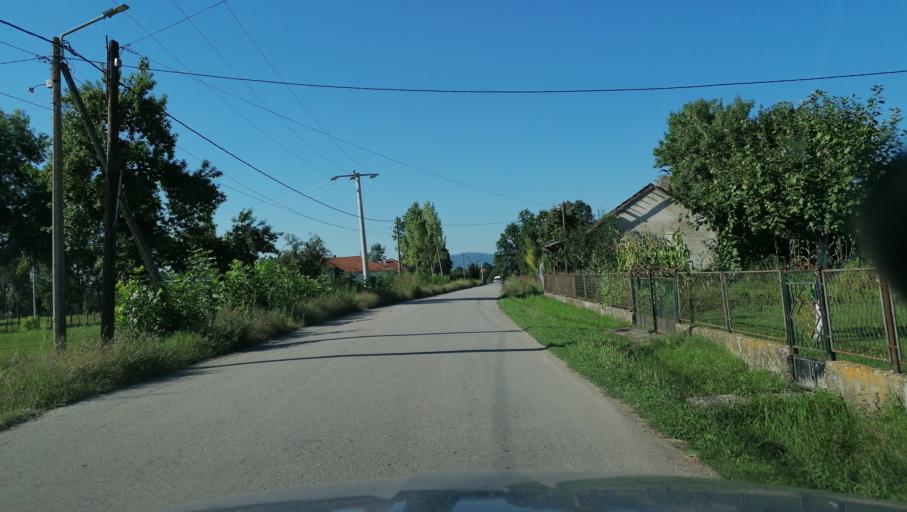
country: RS
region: Central Serbia
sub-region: Raski Okrug
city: Kraljevo
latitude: 43.8332
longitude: 20.5948
